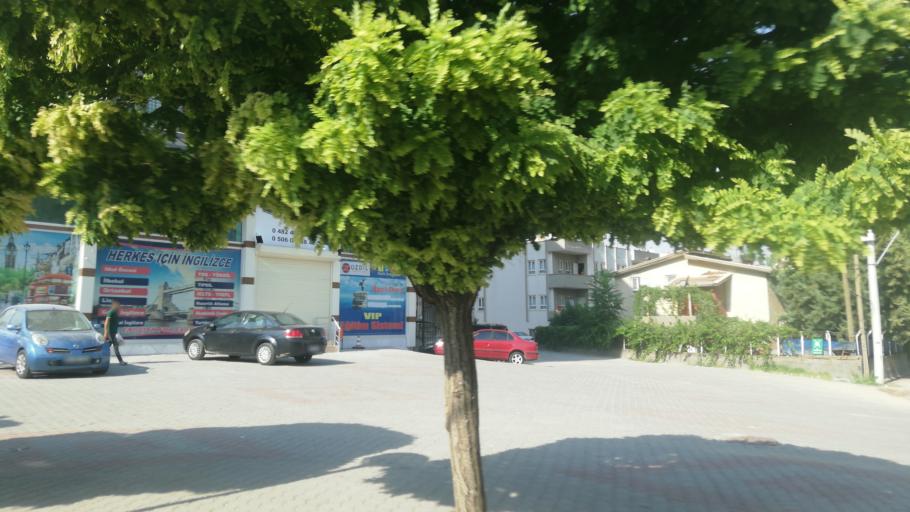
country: TR
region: Mardin
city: Midyat
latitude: 37.4320
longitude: 41.3364
